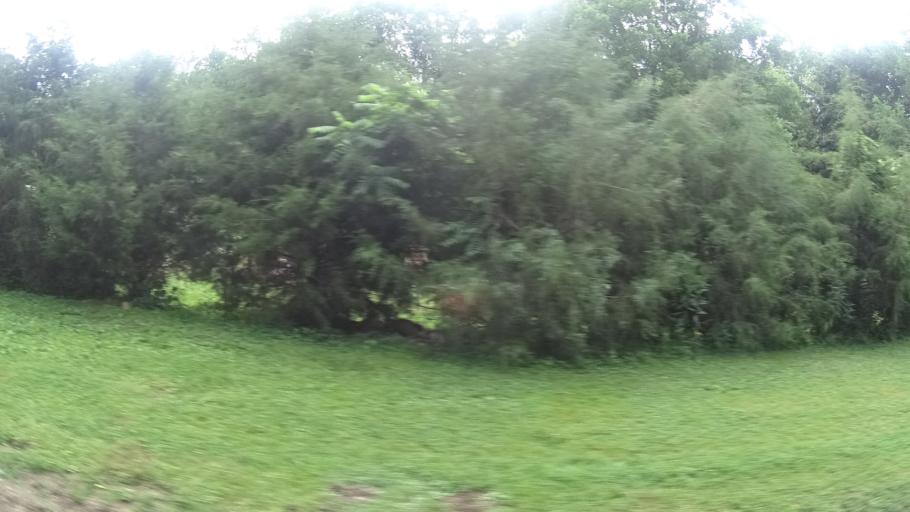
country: US
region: Ohio
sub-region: Erie County
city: Milan
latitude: 41.3011
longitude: -82.5138
